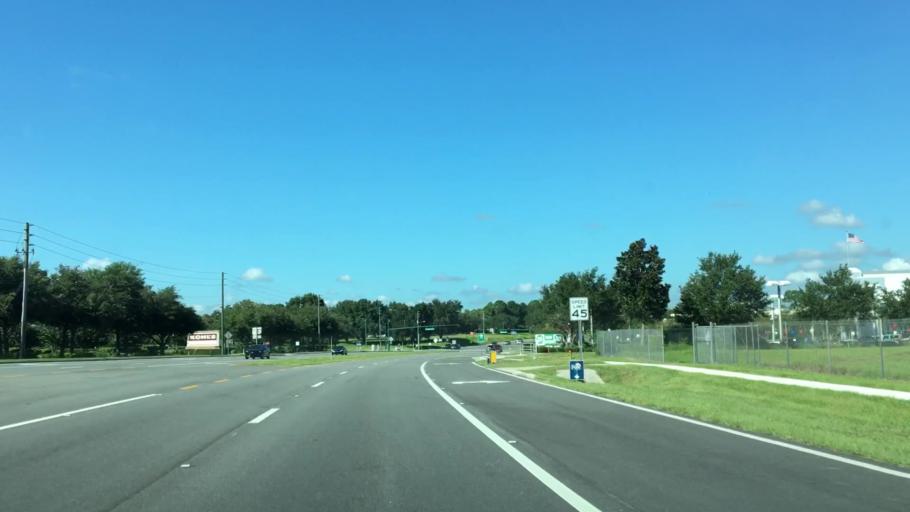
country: US
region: Florida
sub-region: Seminole County
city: Lake Mary
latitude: 28.7962
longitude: -81.3335
